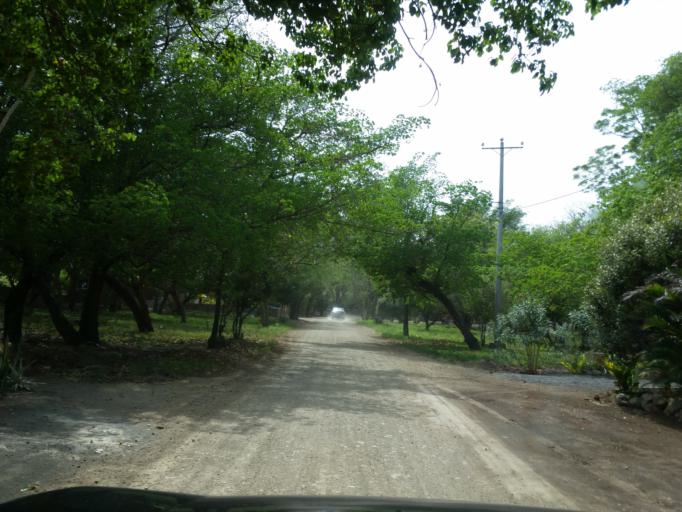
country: NI
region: Rivas
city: Tola
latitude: 11.4094
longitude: -86.0529
